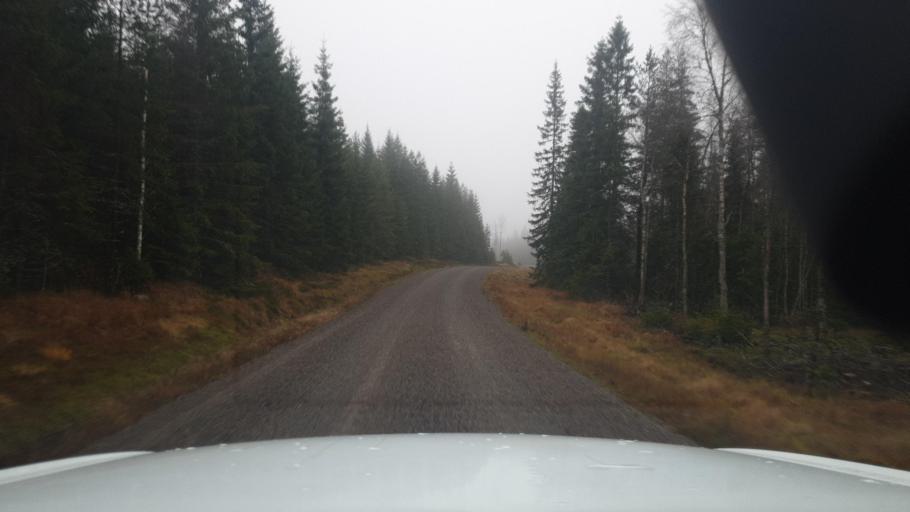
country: SE
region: Vaermland
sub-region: Eda Kommun
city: Charlottenberg
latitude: 60.0768
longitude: 12.6203
